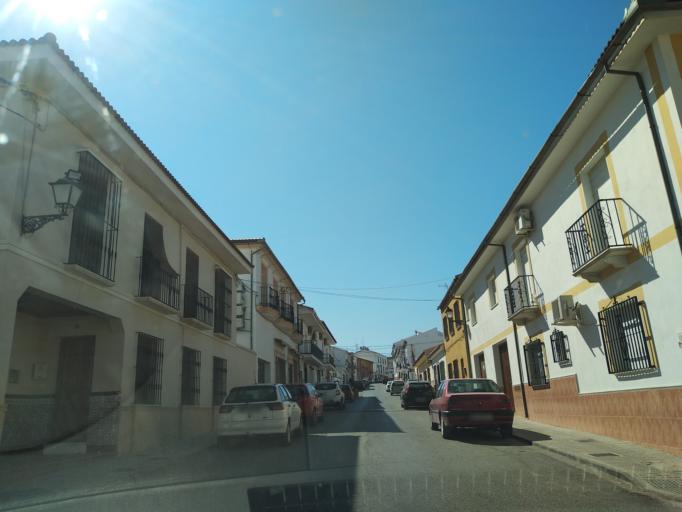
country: ES
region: Andalusia
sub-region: Provincia de Malaga
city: Mollina
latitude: 37.1275
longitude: -4.6573
